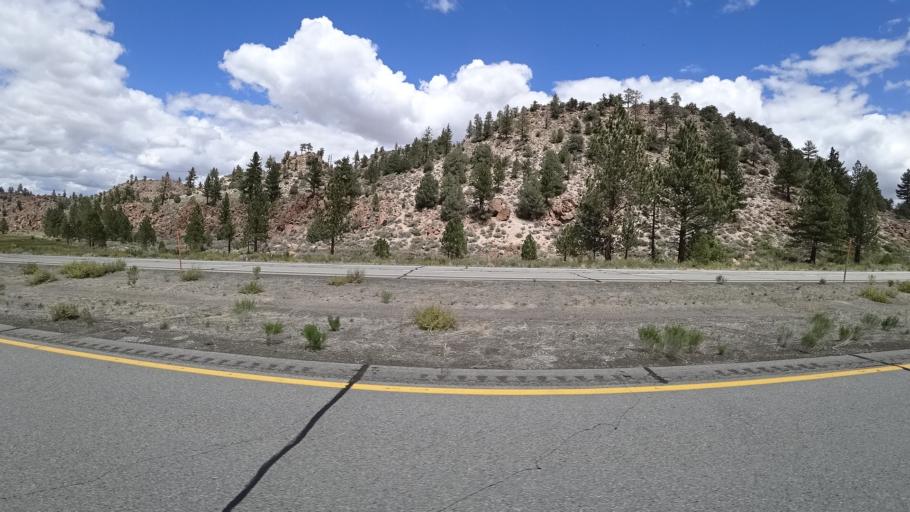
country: US
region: California
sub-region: Mono County
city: Mammoth Lakes
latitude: 37.5656
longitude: -118.6879
